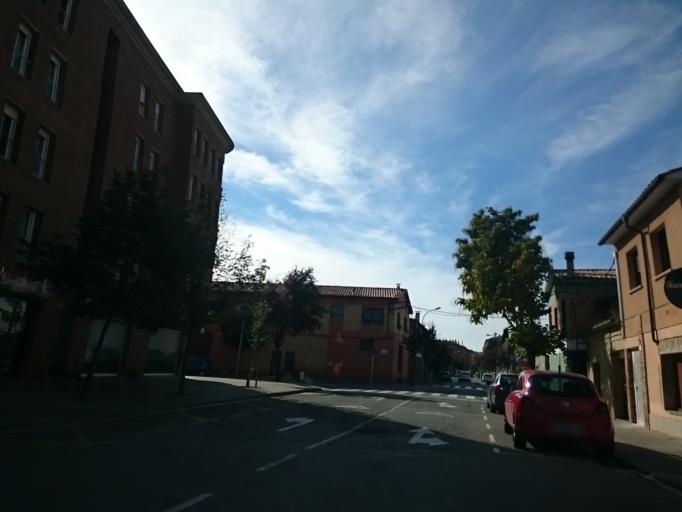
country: ES
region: Catalonia
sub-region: Provincia de Barcelona
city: Vic
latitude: 41.9203
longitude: 2.2571
